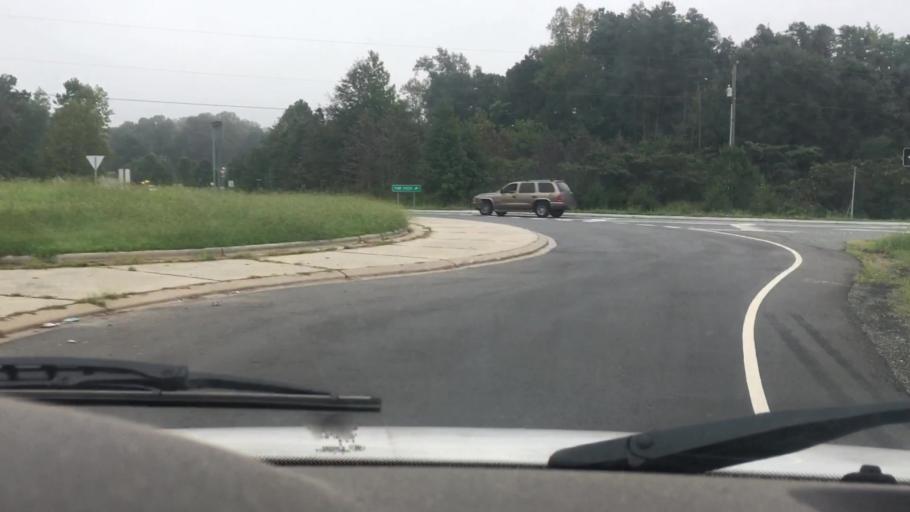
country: US
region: North Carolina
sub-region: Gaston County
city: Mount Holly
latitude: 35.2736
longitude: -80.9650
